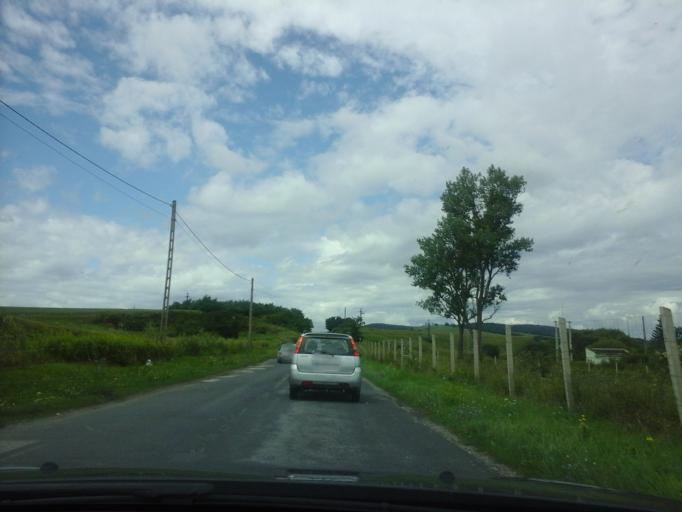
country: HU
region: Borsod-Abauj-Zemplen
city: Sajokaza
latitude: 48.3229
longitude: 20.6114
